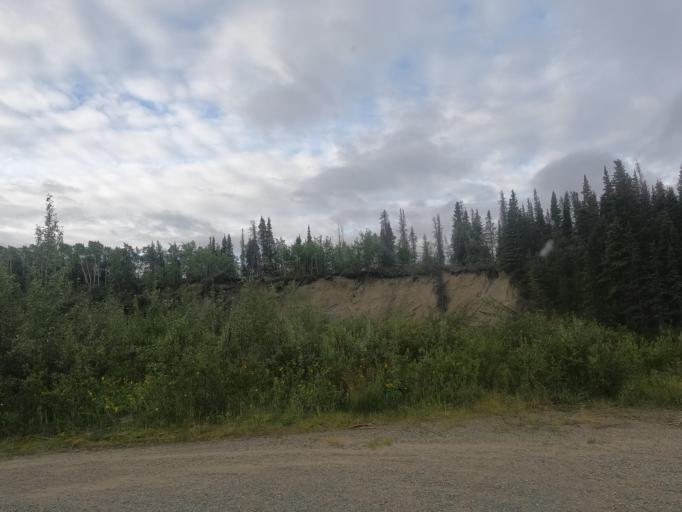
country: CA
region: Yukon
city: Haines Junction
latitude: 60.1108
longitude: -136.9318
